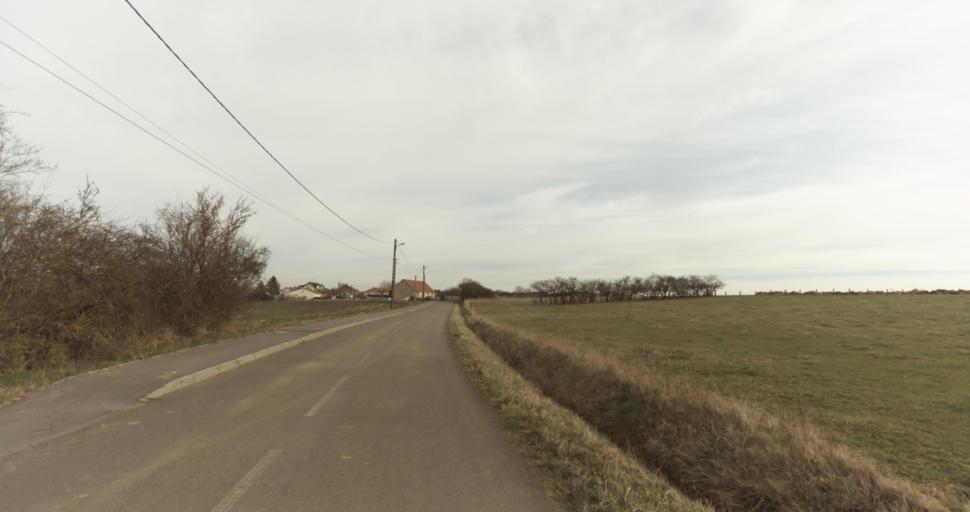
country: FR
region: Lorraine
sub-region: Departement de Meurthe-et-Moselle
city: Jarny
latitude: 49.1399
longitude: 5.8667
